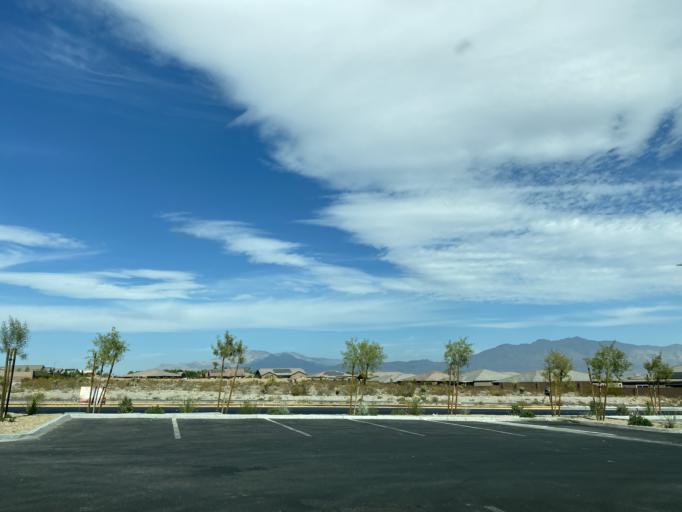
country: US
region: Nevada
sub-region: Clark County
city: Summerlin South
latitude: 36.2844
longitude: -115.3123
